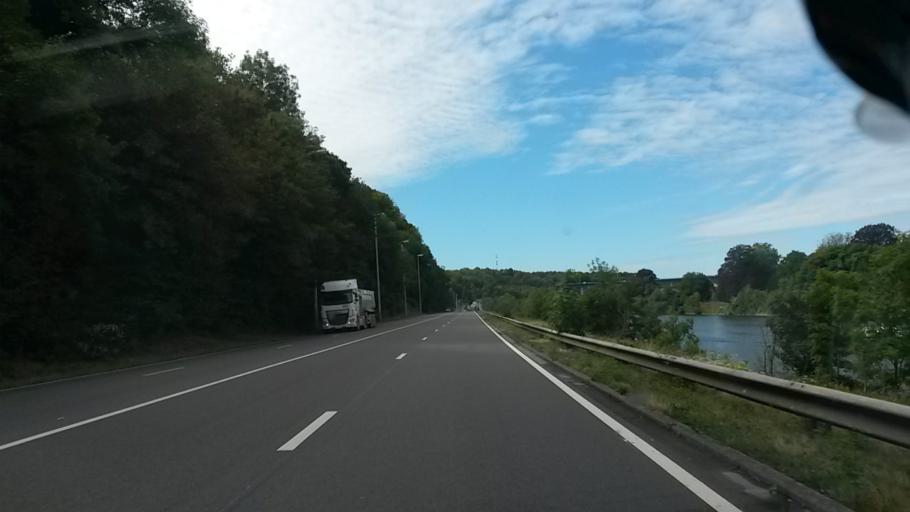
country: BE
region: Wallonia
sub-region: Province de Namur
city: Namur
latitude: 50.4717
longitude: 4.9321
